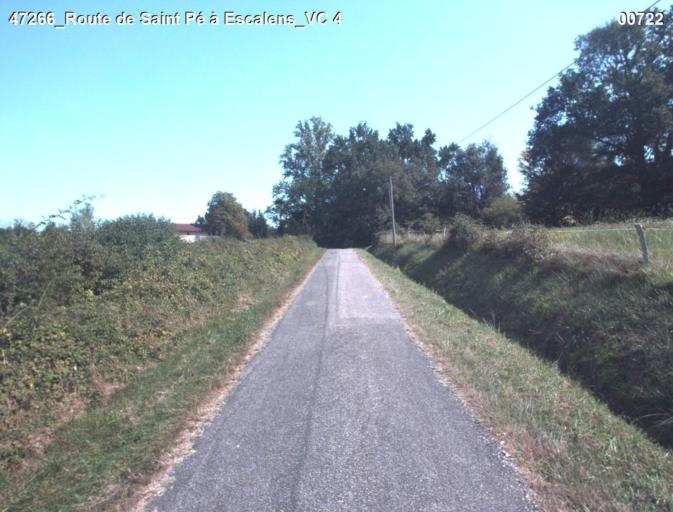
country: FR
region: Aquitaine
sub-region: Departement des Landes
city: Gabarret
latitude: 44.0023
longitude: 0.0692
